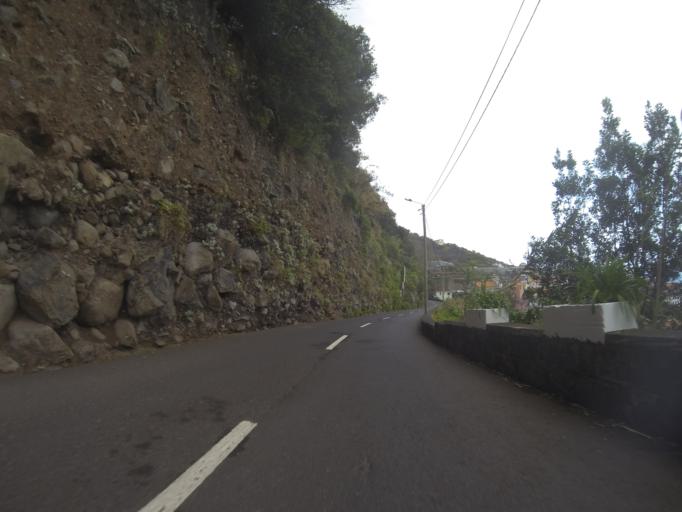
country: PT
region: Madeira
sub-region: Sao Vicente
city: Sao Vicente
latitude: 32.8212
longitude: -17.1052
